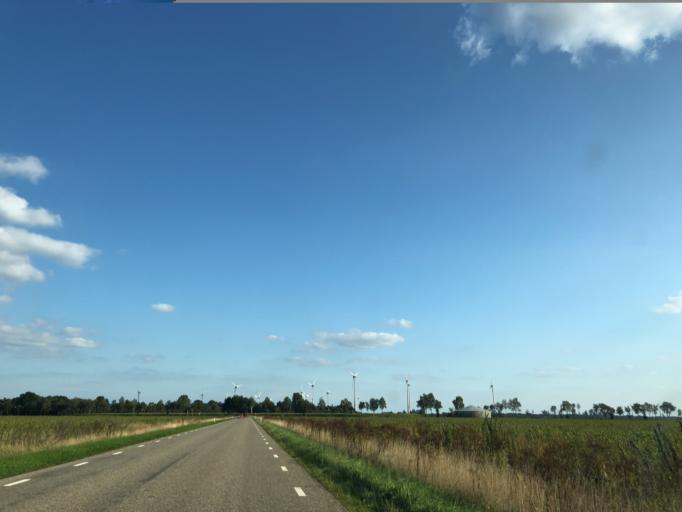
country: NL
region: Groningen
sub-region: Gemeente Vlagtwedde
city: Sellingen
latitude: 53.0004
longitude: 7.1883
